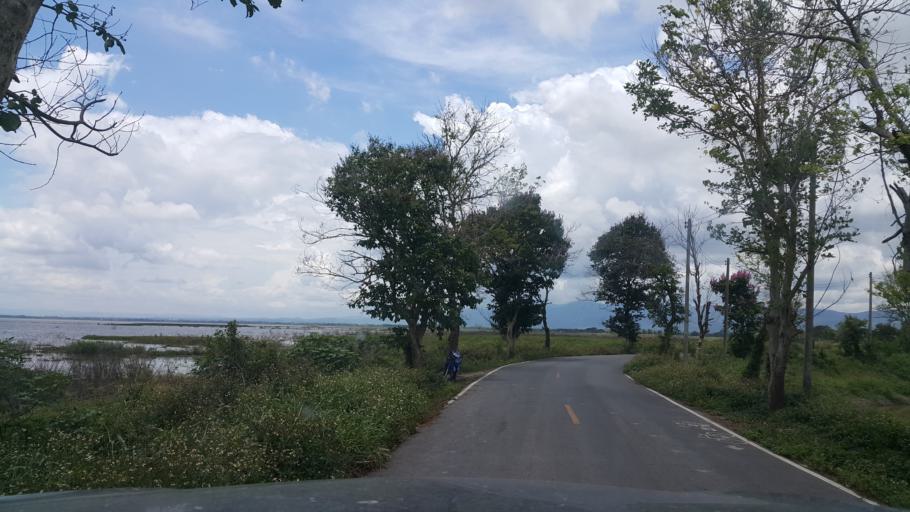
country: TH
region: Phayao
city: Phayao
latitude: 19.1891
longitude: 99.8571
